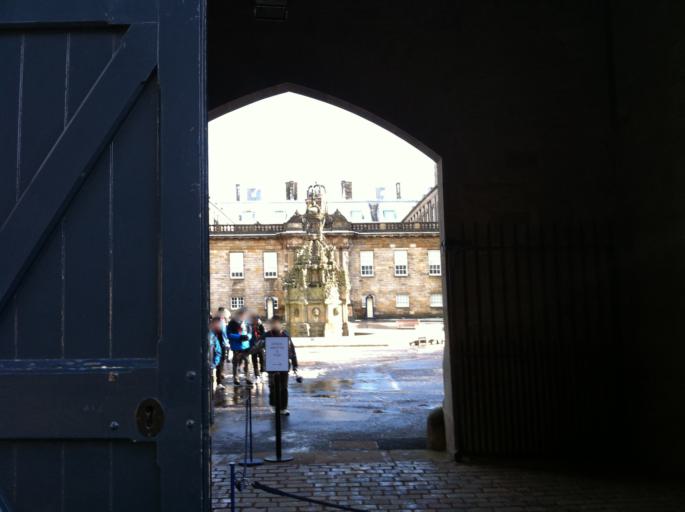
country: GB
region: Scotland
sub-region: Edinburgh
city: Edinburgh
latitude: 55.9524
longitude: -3.1734
